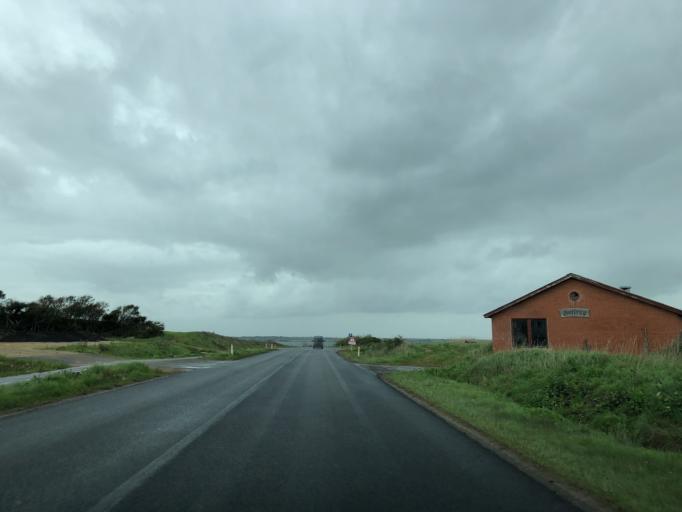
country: DK
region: Central Jutland
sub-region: Struer Kommune
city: Struer
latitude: 56.5535
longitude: 8.5581
